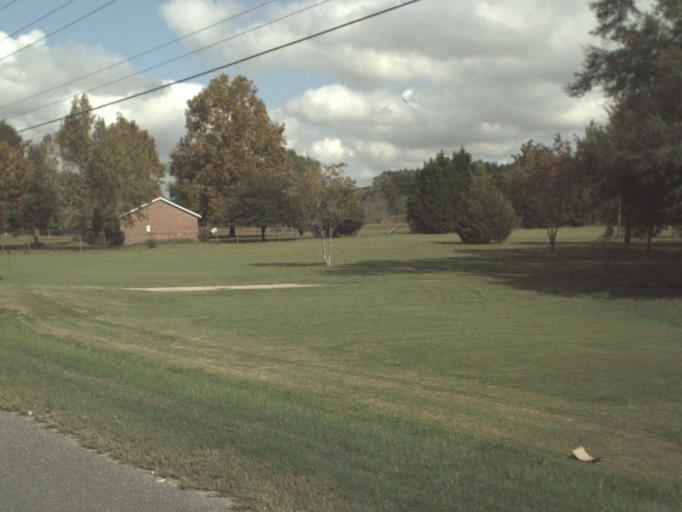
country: US
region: Florida
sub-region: Jackson County
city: Malone
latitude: 30.8827
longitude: -85.1613
